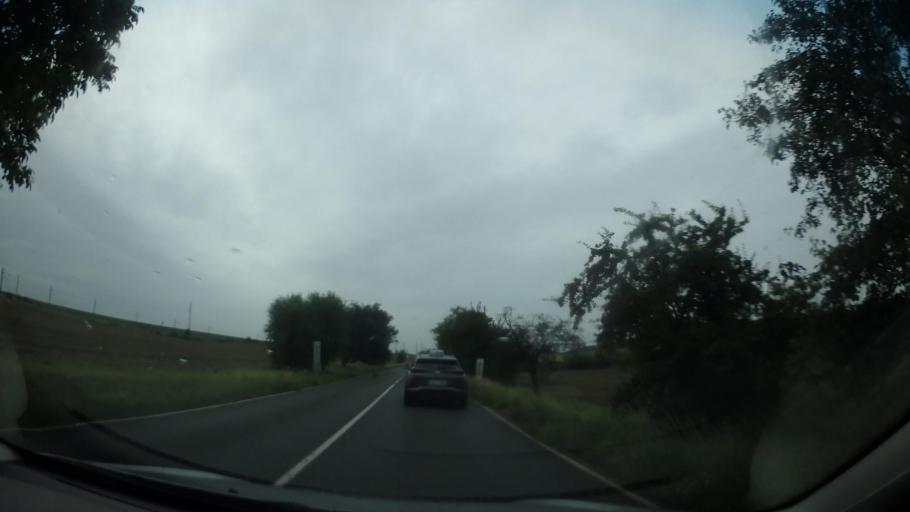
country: CZ
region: Central Bohemia
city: Milovice
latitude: 50.2210
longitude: 14.8753
